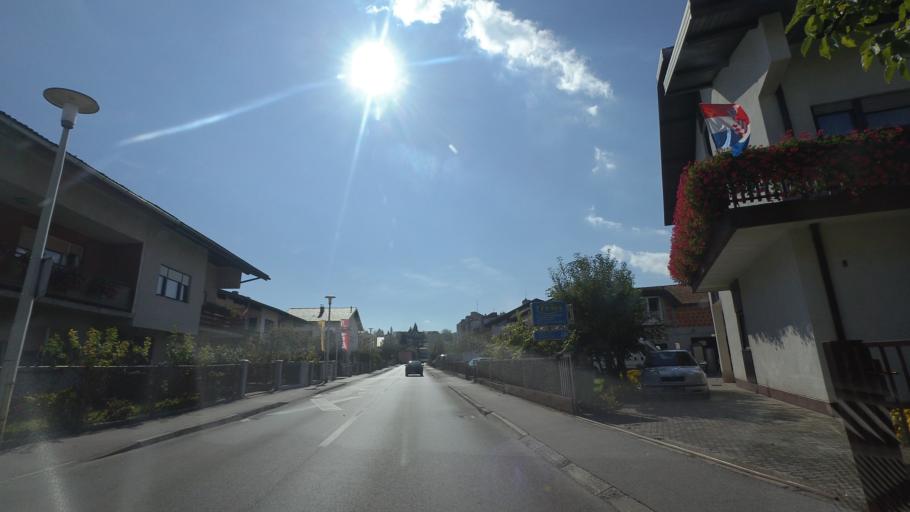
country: HR
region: Karlovacka
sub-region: Grad Karlovac
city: Karlovac
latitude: 45.4822
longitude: 15.5455
